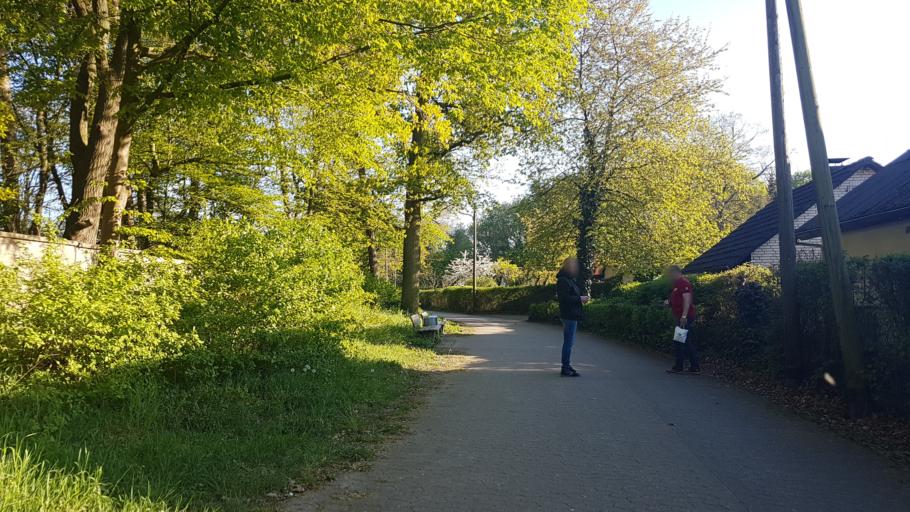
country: DE
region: Lower Saxony
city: Hannover
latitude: 52.3962
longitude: 9.7847
